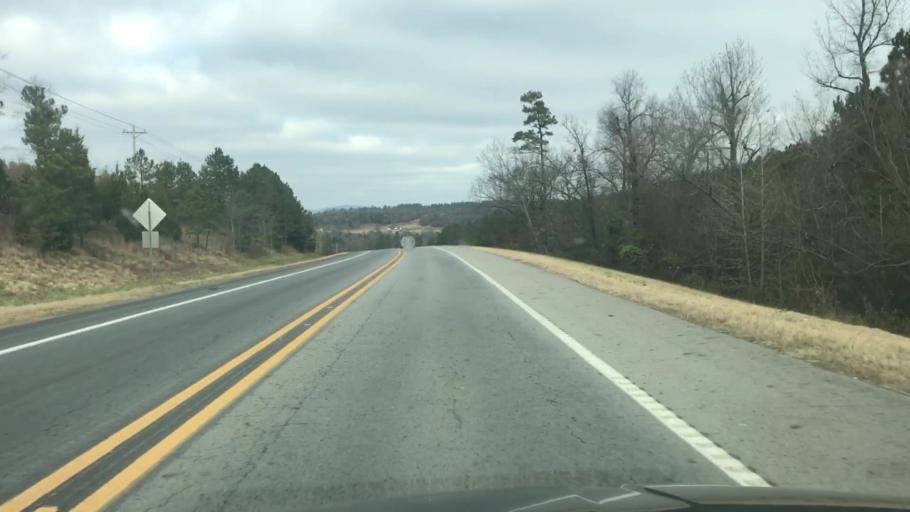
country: US
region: Arkansas
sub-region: Scott County
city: Waldron
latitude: 34.8423
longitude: -94.0543
